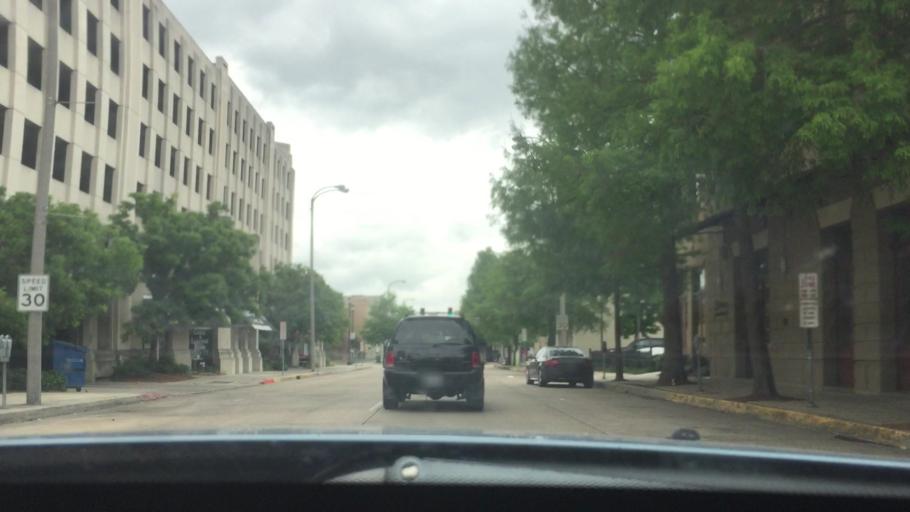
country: US
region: Louisiana
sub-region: West Baton Rouge Parish
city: Port Allen
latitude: 30.4515
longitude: -91.1859
